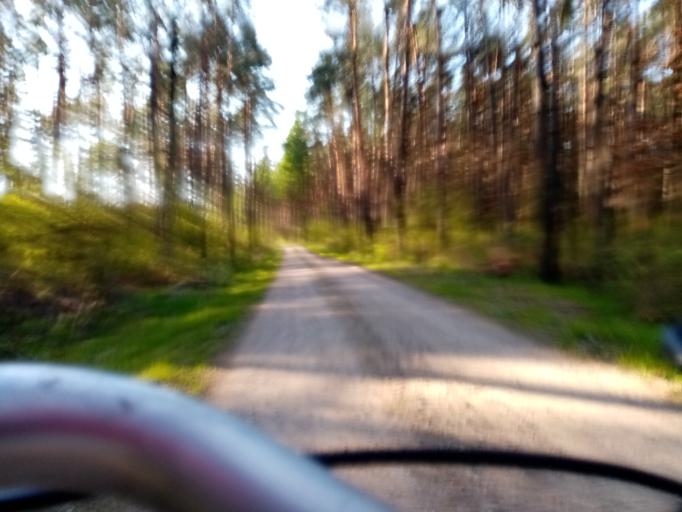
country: PL
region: Kujawsko-Pomorskie
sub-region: Powiat brodnicki
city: Gorzno
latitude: 53.1669
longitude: 19.6746
